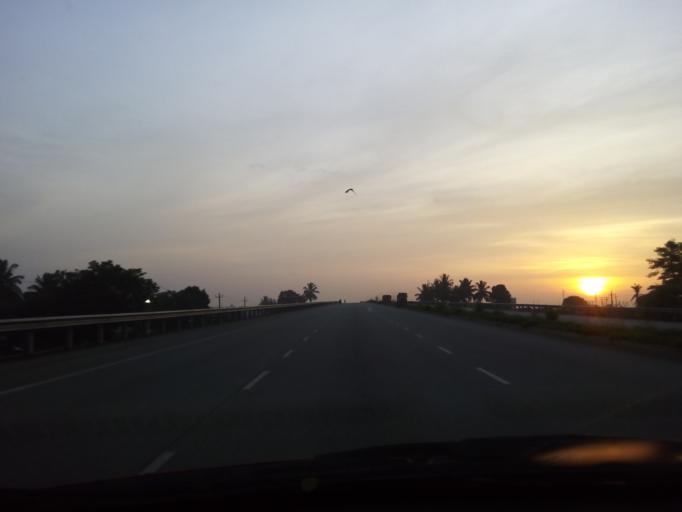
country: IN
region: Karnataka
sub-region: Bangalore Rural
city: Devanhalli
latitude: 13.2135
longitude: 77.6745
